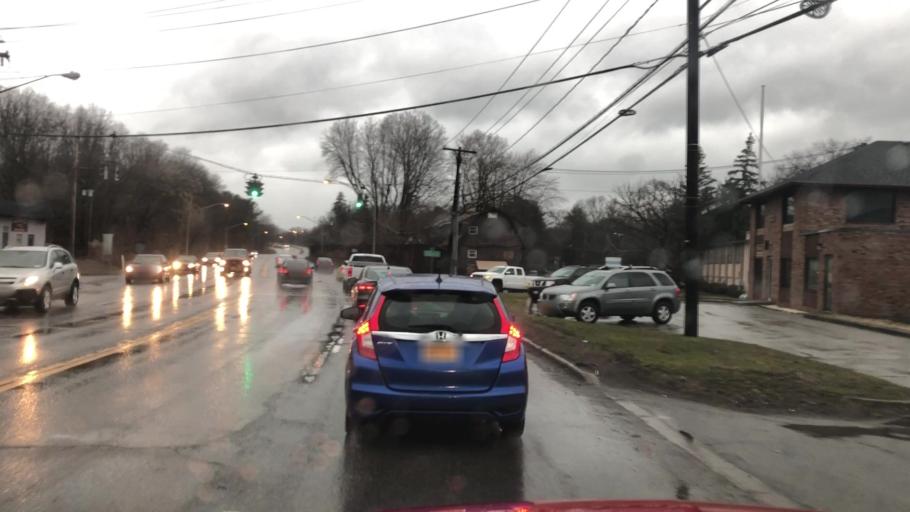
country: US
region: New York
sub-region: Monroe County
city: East Rochester
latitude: 43.1167
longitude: -77.4985
